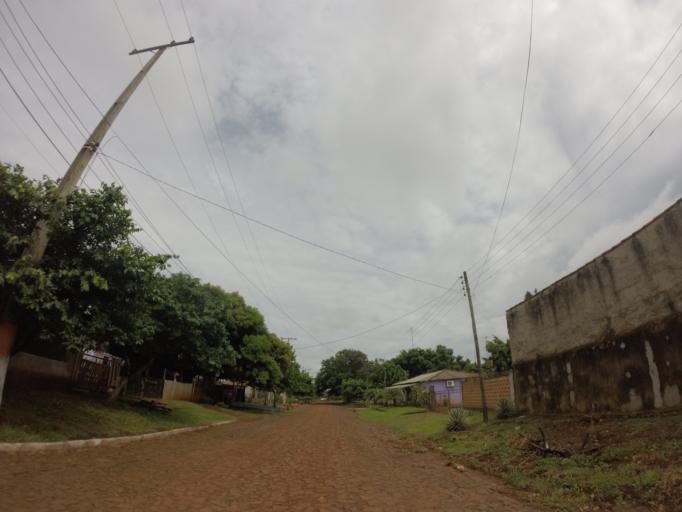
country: PY
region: Alto Parana
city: Ciudad del Este
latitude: -25.3829
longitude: -54.6558
